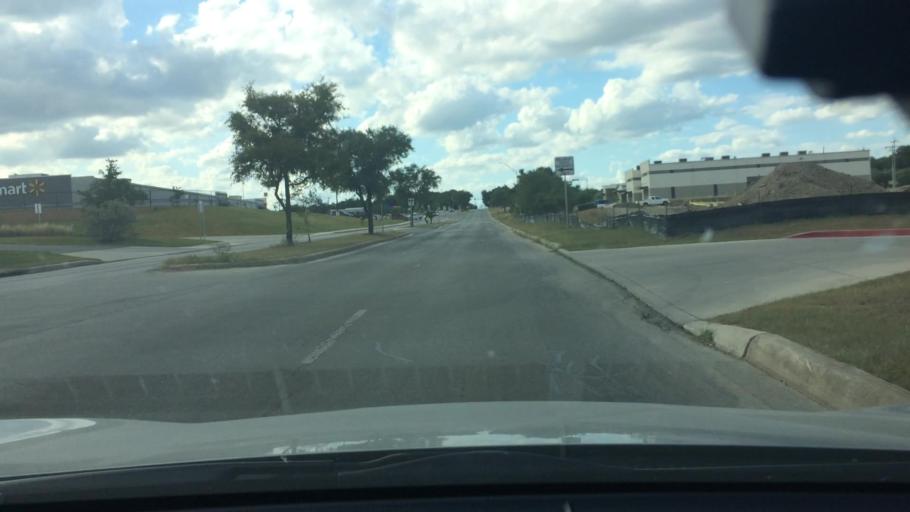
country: US
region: Texas
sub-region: Bexar County
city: Universal City
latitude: 29.5468
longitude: -98.3060
